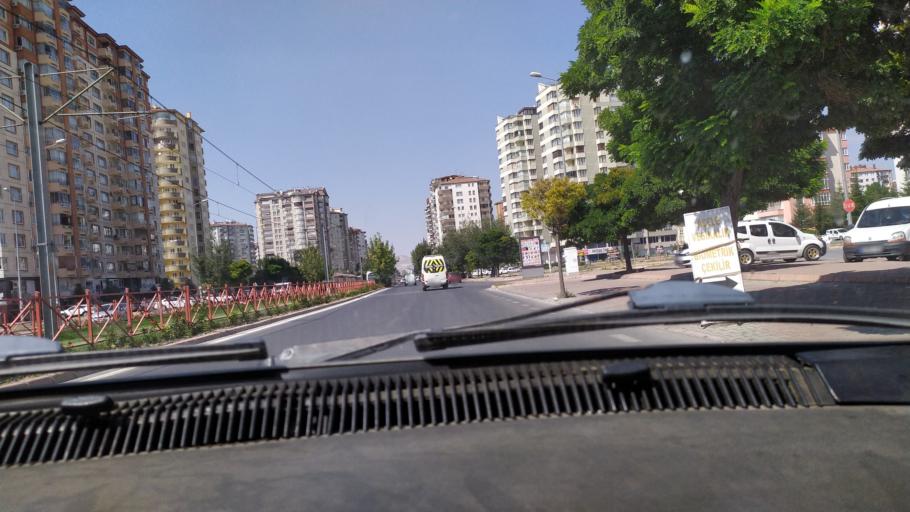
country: TR
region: Kayseri
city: Kayseri
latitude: 38.7258
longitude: 35.5267
